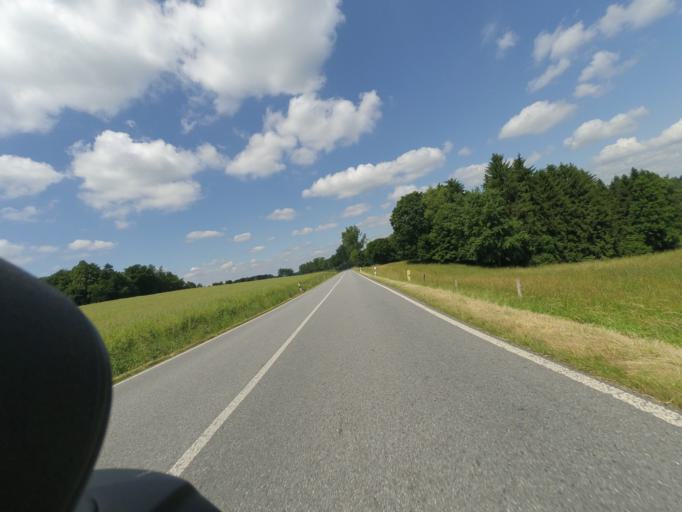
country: DE
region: Saxony
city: Bad Schandau
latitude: 50.9364
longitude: 14.1949
